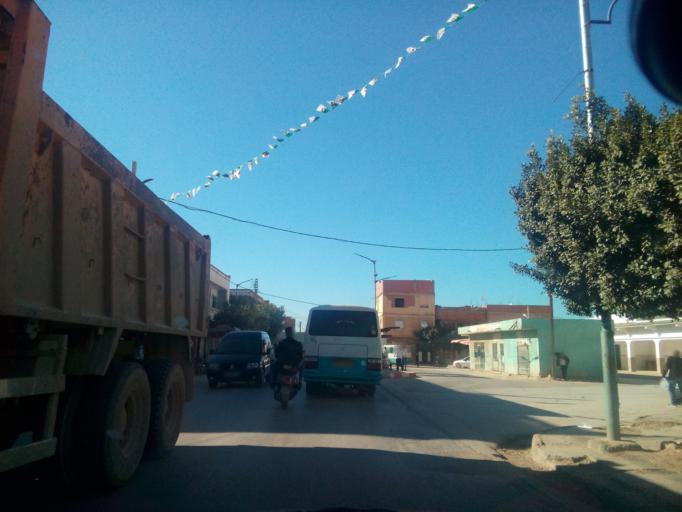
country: DZ
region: Relizane
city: Djidiouia
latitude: 35.9296
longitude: 0.8310
